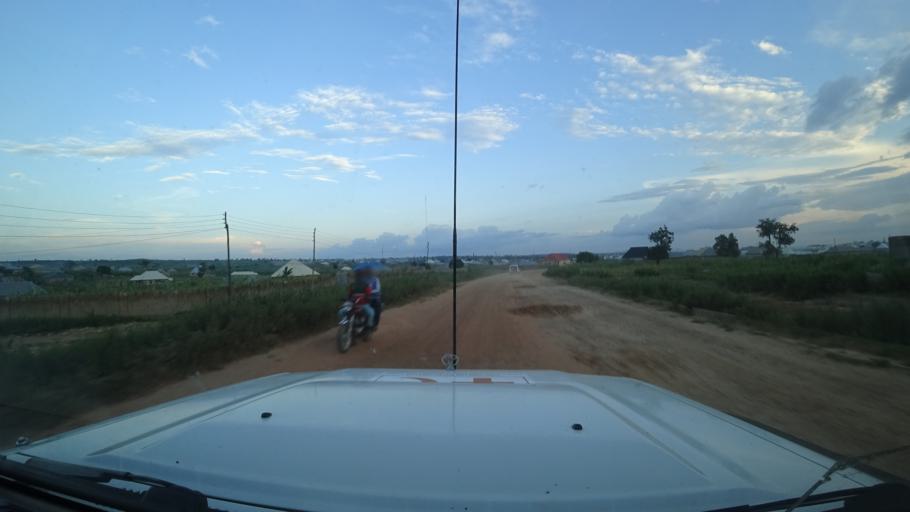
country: NG
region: Niger
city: Minna
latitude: 9.6489
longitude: 6.5801
